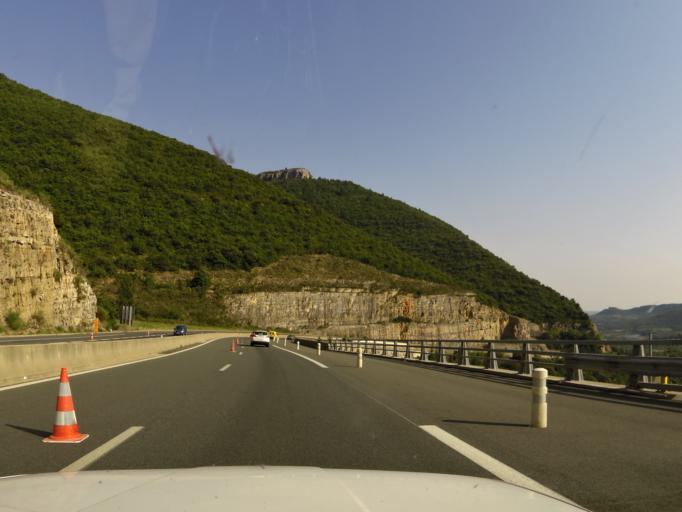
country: FR
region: Languedoc-Roussillon
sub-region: Departement de l'Herault
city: Lodeve
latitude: 43.8069
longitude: 3.3259
